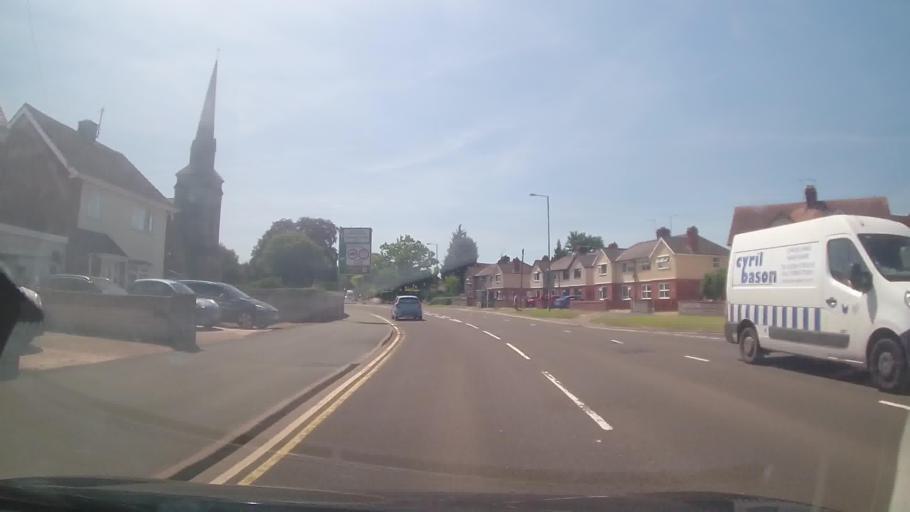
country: GB
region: England
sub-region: Herefordshire
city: Hereford
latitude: 52.0458
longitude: -2.7207
